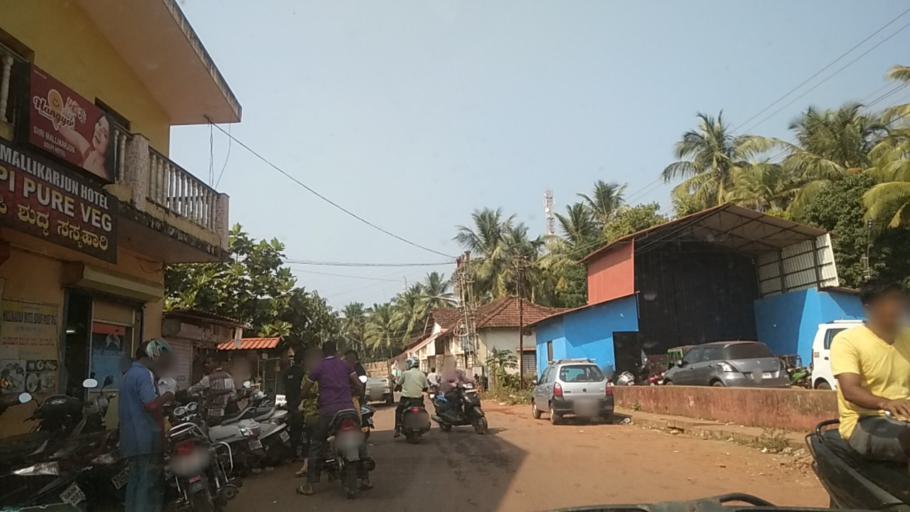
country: IN
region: Goa
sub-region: South Goa
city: Kankon
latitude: 15.0110
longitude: 74.0362
